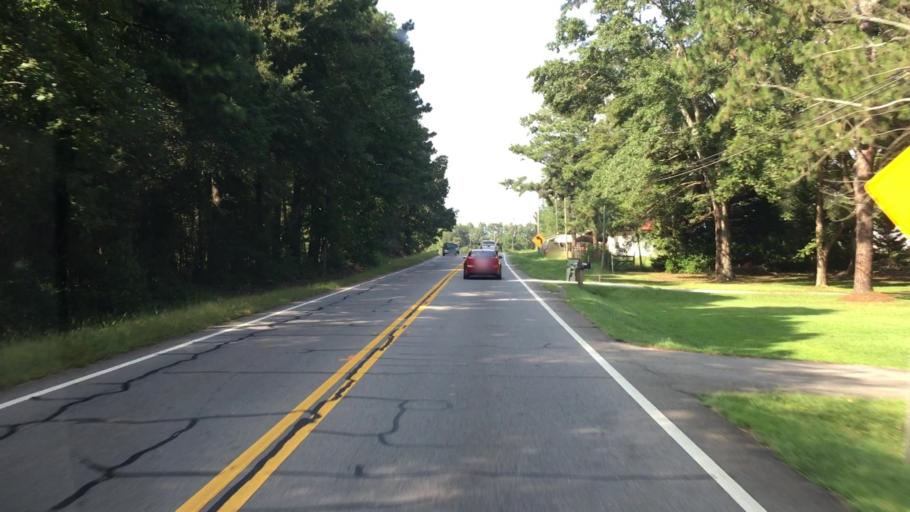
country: US
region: Georgia
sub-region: Walton County
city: Monroe
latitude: 33.7553
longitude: -83.7005
